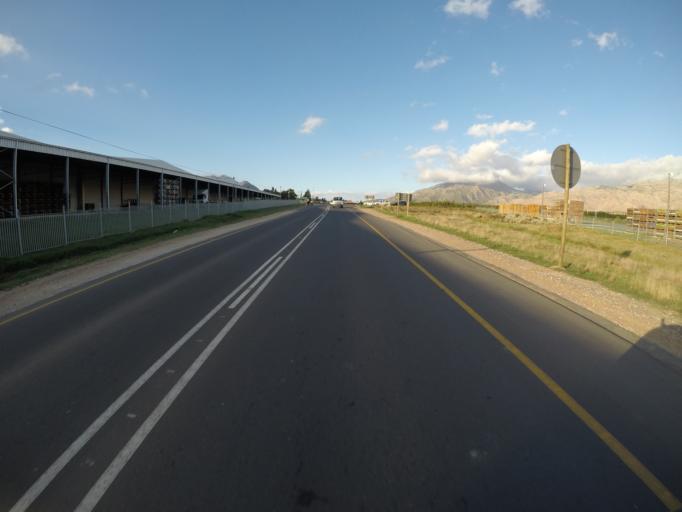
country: ZA
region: Western Cape
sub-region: Overberg District Municipality
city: Caledon
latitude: -33.9975
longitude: 19.2848
